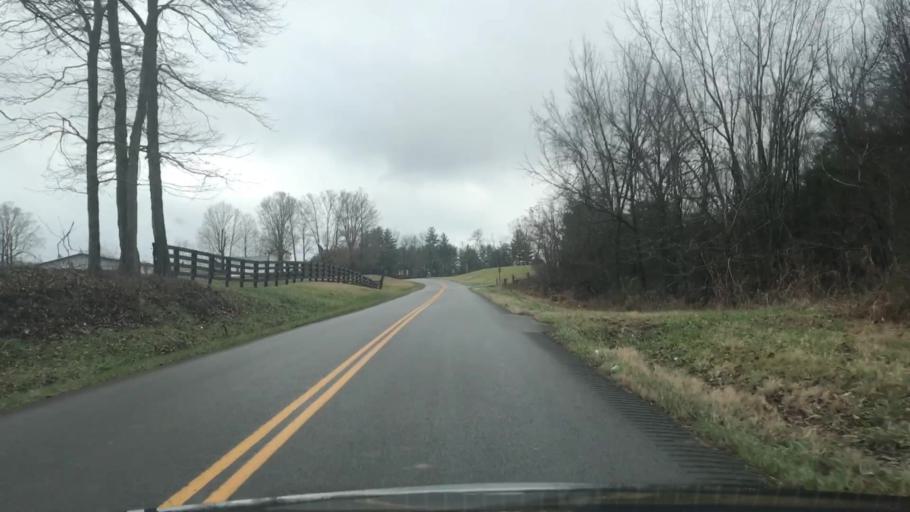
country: US
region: Kentucky
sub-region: Monroe County
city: Tompkinsville
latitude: 36.7251
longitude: -85.7097
